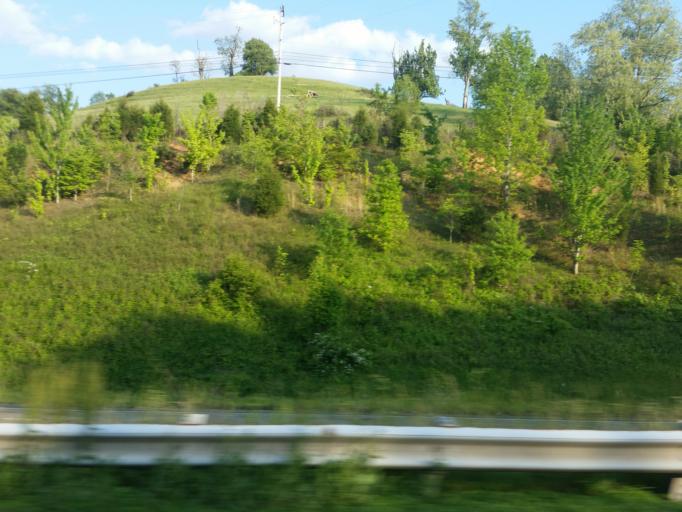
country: US
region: Virginia
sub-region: Russell County
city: Honaker
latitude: 36.9353
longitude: -81.9855
